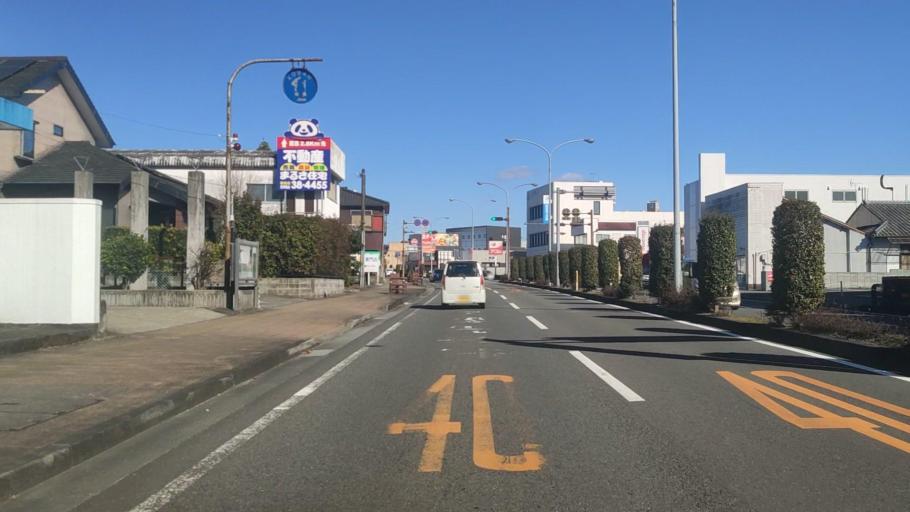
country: JP
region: Miyazaki
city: Miyakonojo
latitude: 31.7297
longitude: 131.0673
